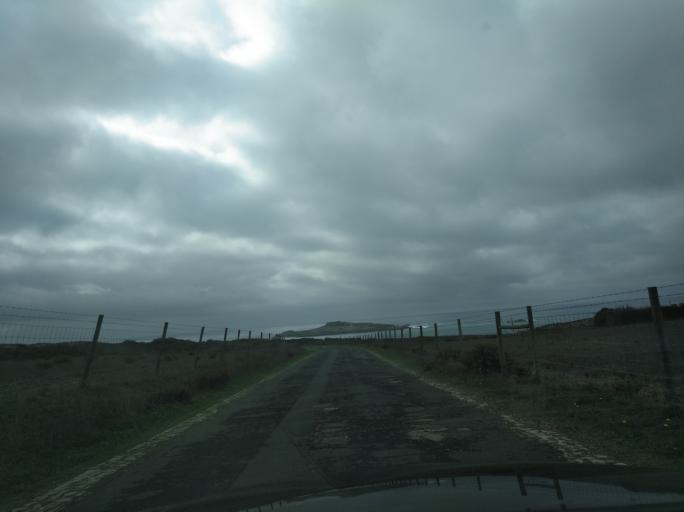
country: PT
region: Setubal
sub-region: Sines
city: Porto Covo
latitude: 37.8391
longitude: -8.7861
